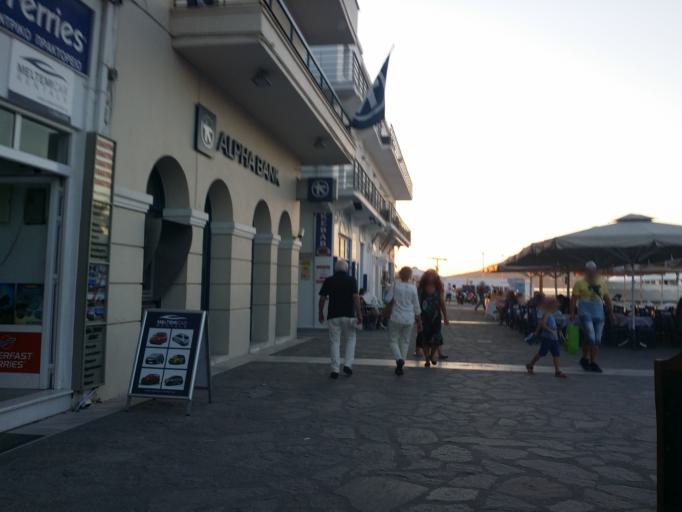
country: GR
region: South Aegean
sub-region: Nomos Kykladon
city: Paros
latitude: 37.0858
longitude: 25.1504
